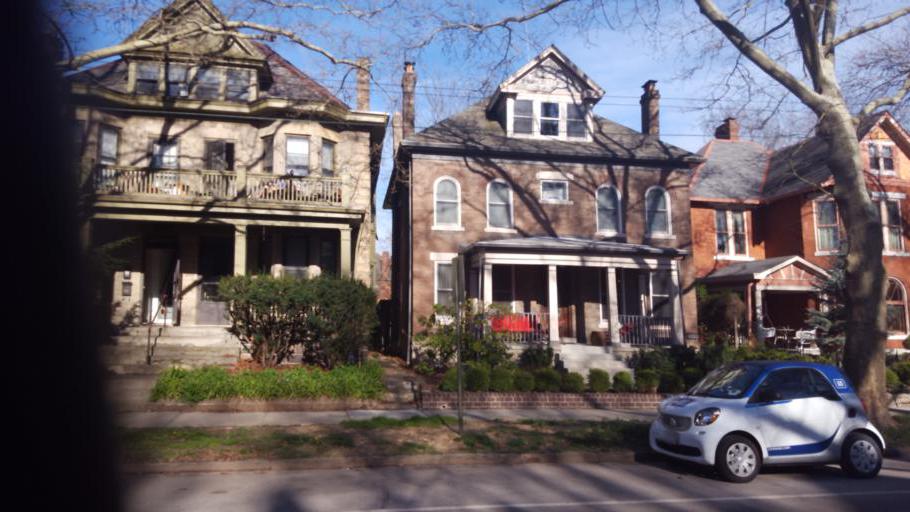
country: US
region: Ohio
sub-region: Franklin County
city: Columbus
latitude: 39.9791
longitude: -83.0115
